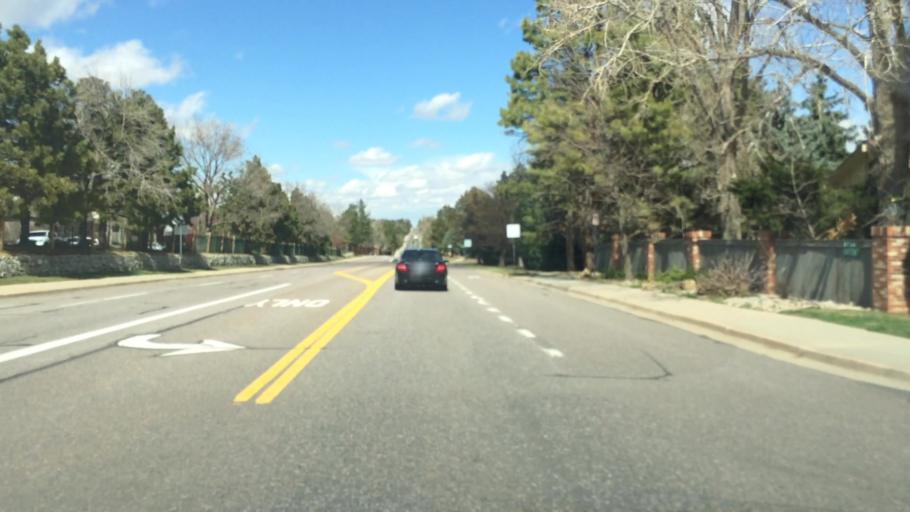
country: US
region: Colorado
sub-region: Arapahoe County
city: Centennial
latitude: 39.6037
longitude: -104.8761
